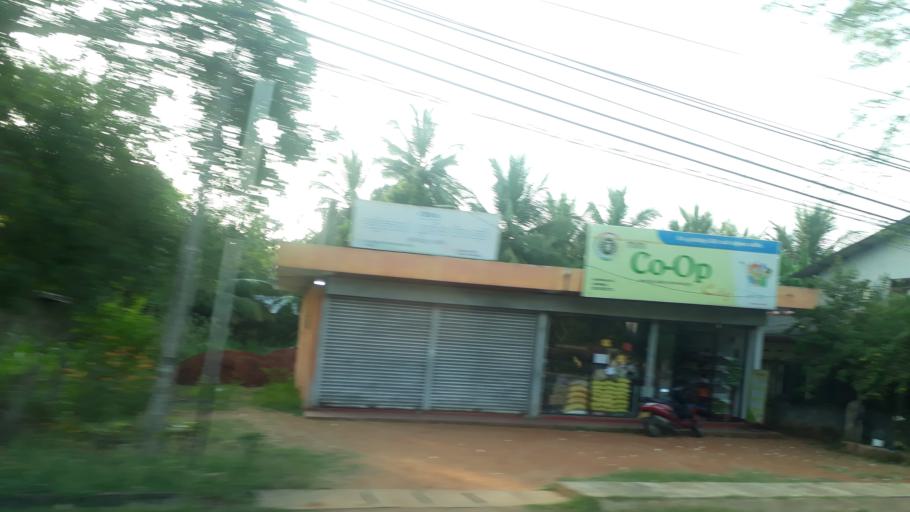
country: LK
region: North Central
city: Anuradhapura
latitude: 8.2991
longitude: 80.3764
